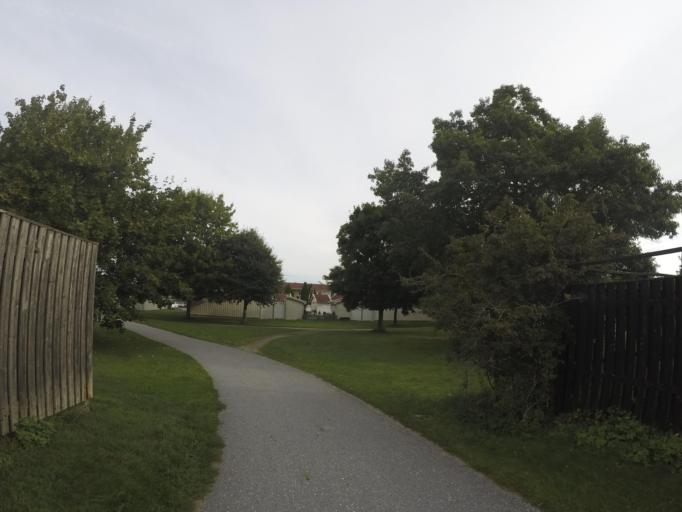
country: SE
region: OErebro
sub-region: Orebro Kommun
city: Orebro
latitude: 59.2645
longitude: 15.2444
